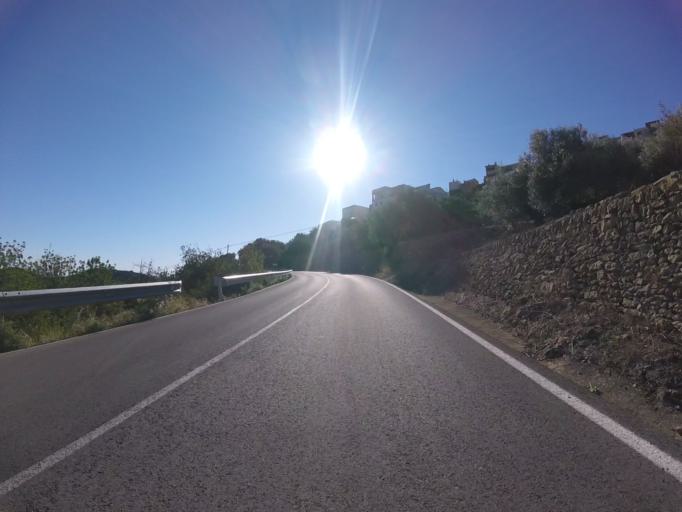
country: ES
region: Valencia
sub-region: Provincia de Castello
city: Cervera del Maestre
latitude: 40.4559
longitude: 0.2772
